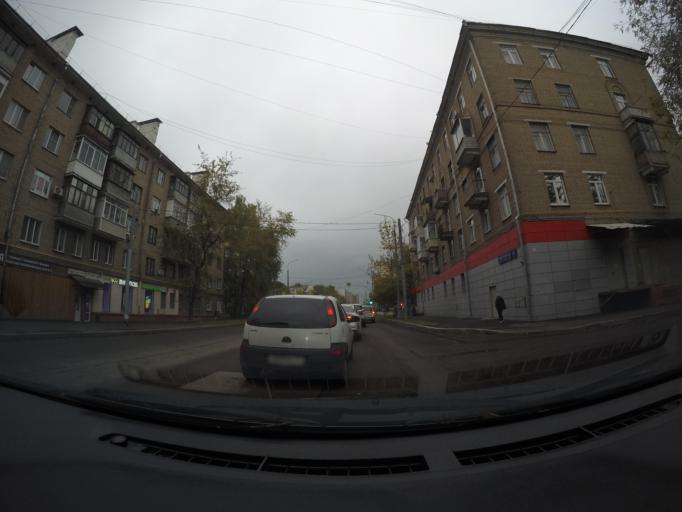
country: RU
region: Moscow
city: Perovo
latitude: 55.7603
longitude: 37.7940
